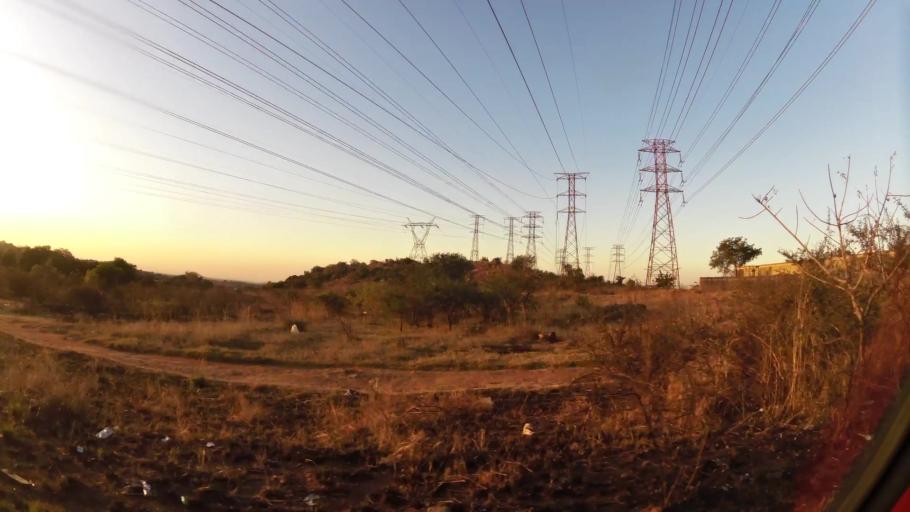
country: ZA
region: North-West
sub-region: Bojanala Platinum District Municipality
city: Rustenburg
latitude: -25.6308
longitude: 27.2036
